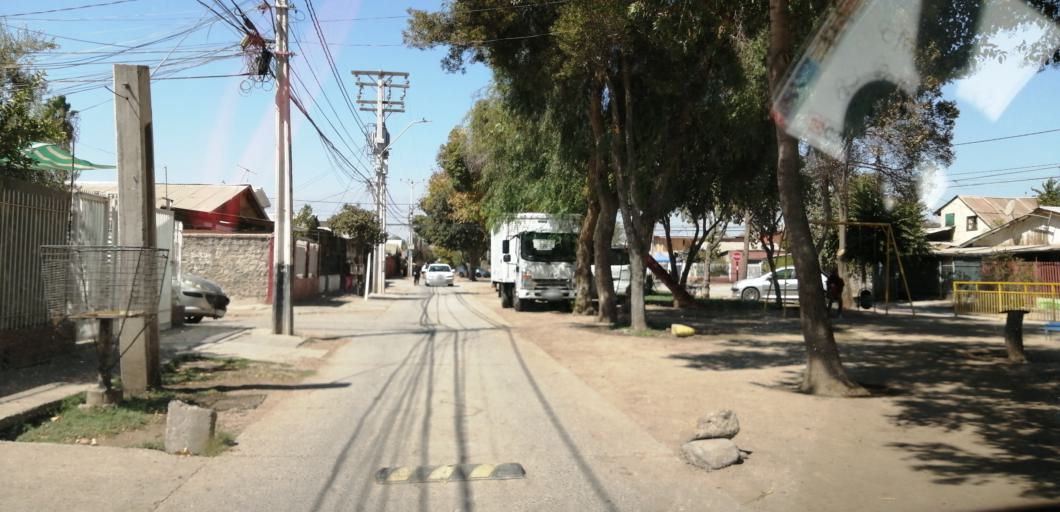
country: CL
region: Santiago Metropolitan
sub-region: Provincia de Santiago
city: Lo Prado
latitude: -33.4487
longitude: -70.7483
